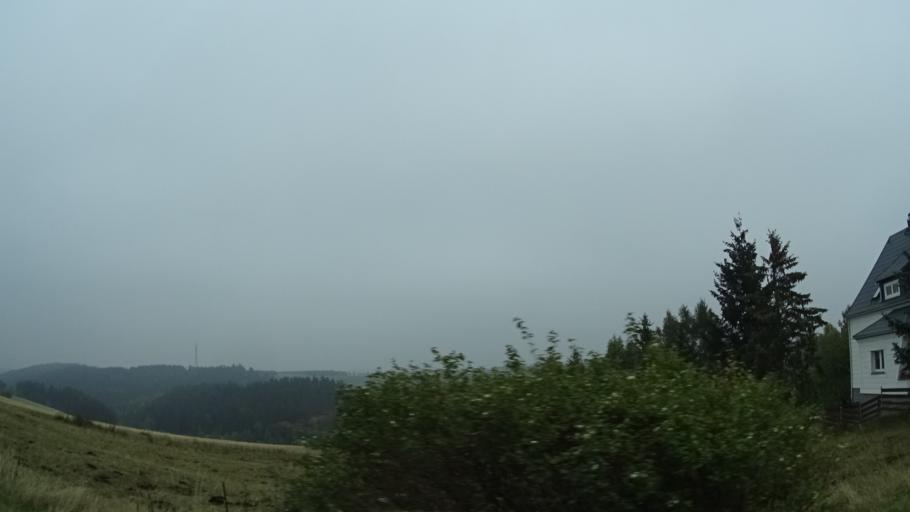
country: DE
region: Thuringia
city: Herschdorf
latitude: 50.6327
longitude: 11.0501
